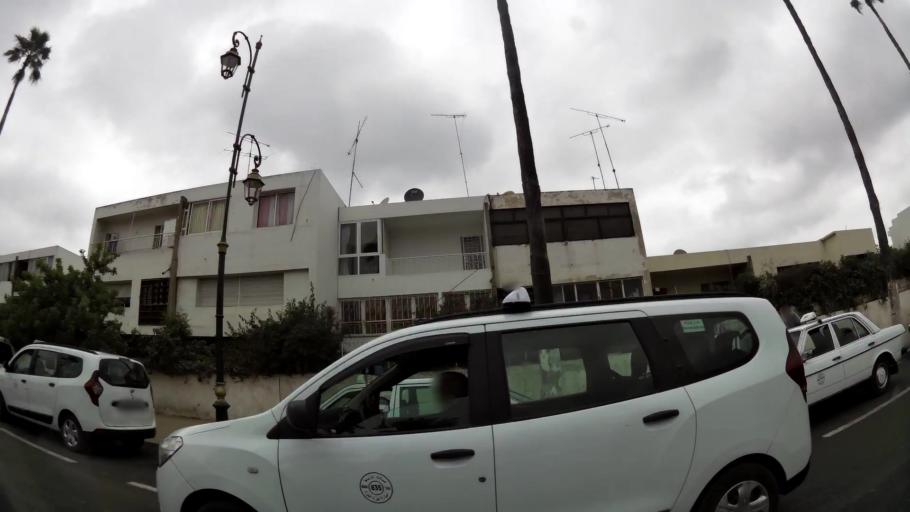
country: MA
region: Rabat-Sale-Zemmour-Zaer
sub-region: Rabat
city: Rabat
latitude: 33.9848
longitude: -6.8247
